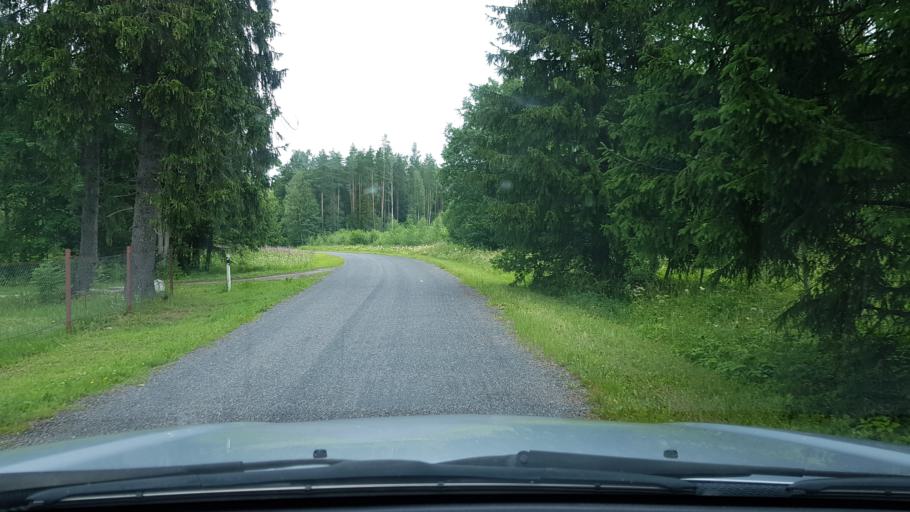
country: EE
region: Ida-Virumaa
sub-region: Narva-Joesuu linn
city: Narva-Joesuu
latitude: 59.3566
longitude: 28.0398
